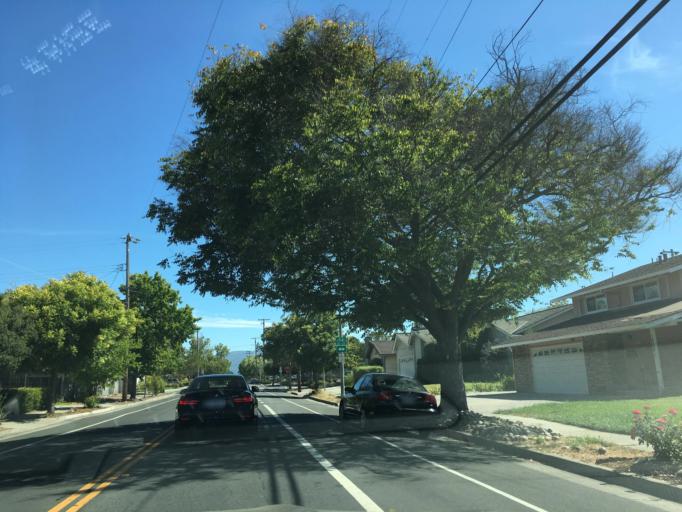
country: US
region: California
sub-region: Santa Clara County
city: Cupertino
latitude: 37.3311
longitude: -122.0232
